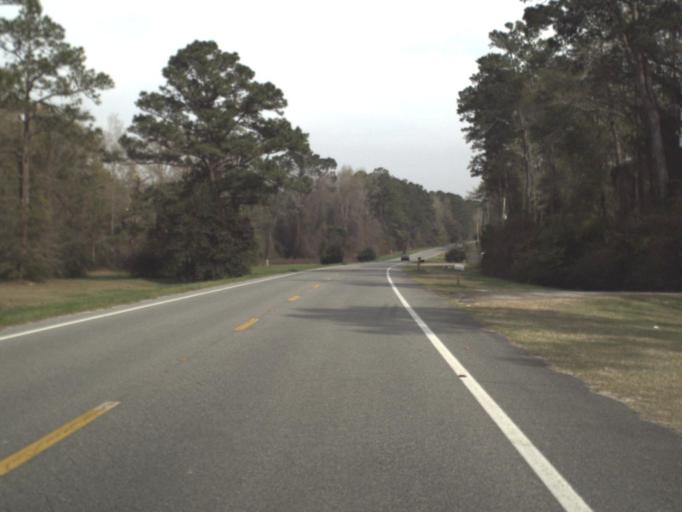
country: US
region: Florida
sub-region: Jefferson County
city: Monticello
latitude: 30.5451
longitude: -83.8512
